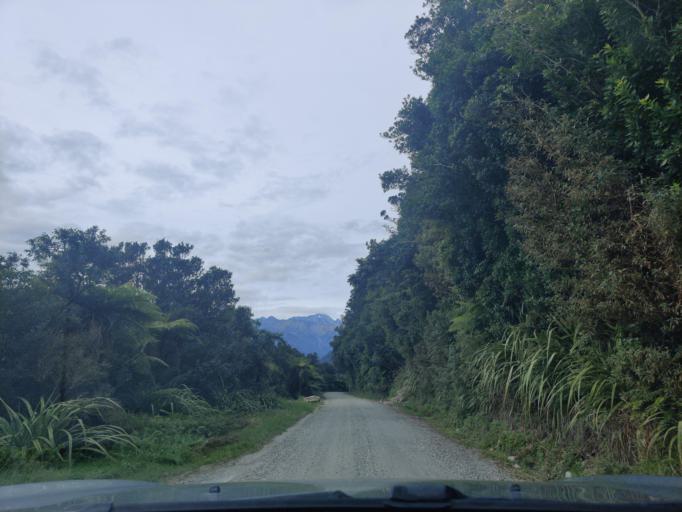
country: NZ
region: West Coast
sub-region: Westland District
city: Hokitika
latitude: -43.2888
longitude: 170.4048
